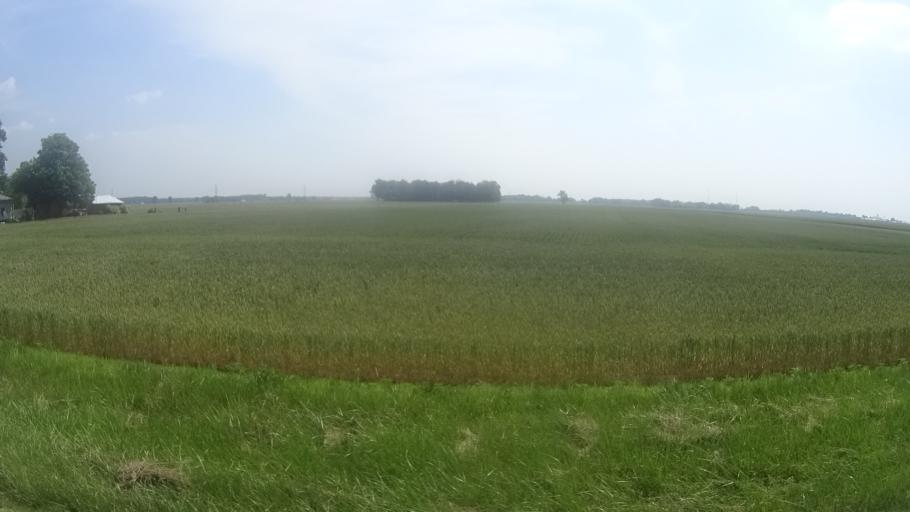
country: US
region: Ohio
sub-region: Huron County
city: Monroeville
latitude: 41.3417
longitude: -82.7236
